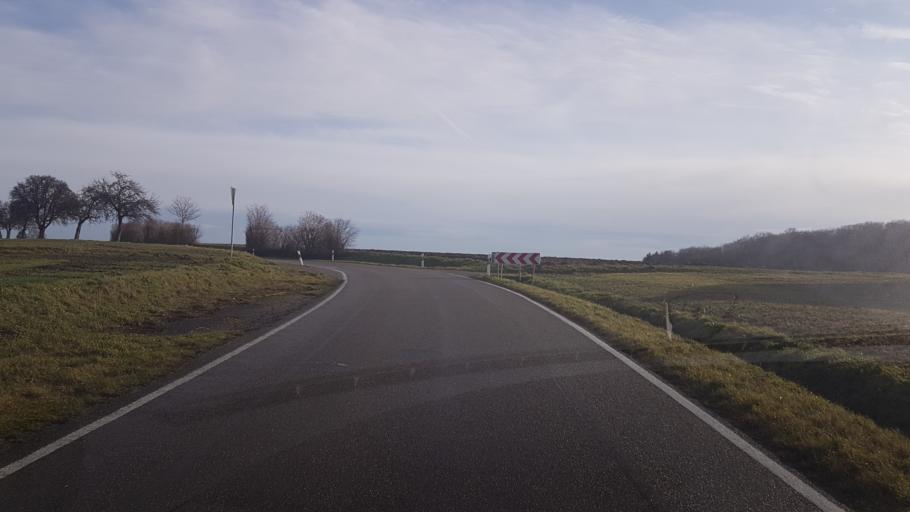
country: DE
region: Baden-Wuerttemberg
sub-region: Regierungsbezirk Stuttgart
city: Kupferzell
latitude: 49.2097
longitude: 9.7173
